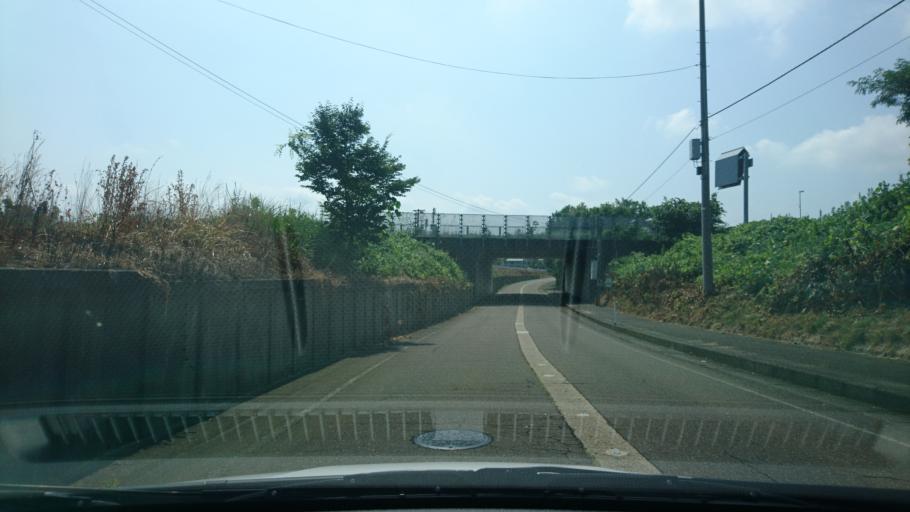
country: JP
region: Niigata
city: Arai
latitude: 37.0567
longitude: 138.2542
